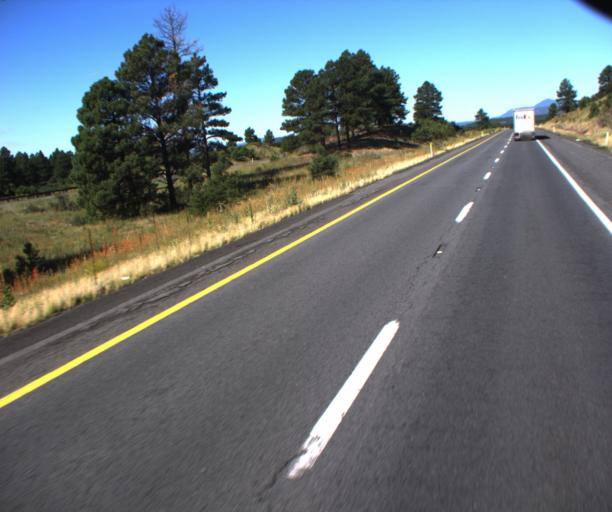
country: US
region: Arizona
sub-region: Coconino County
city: Parks
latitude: 35.2505
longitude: -111.9610
